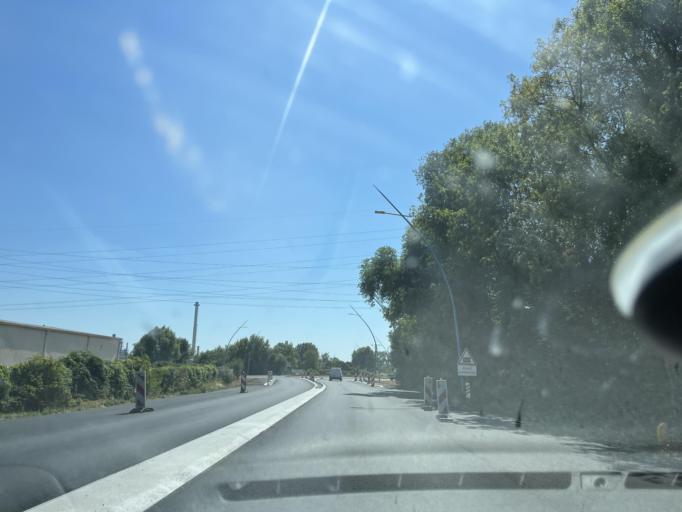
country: FR
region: Haute-Normandie
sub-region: Departement de l'Eure
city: Quillebeuf-sur-Seine
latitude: 49.4943
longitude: 0.5350
